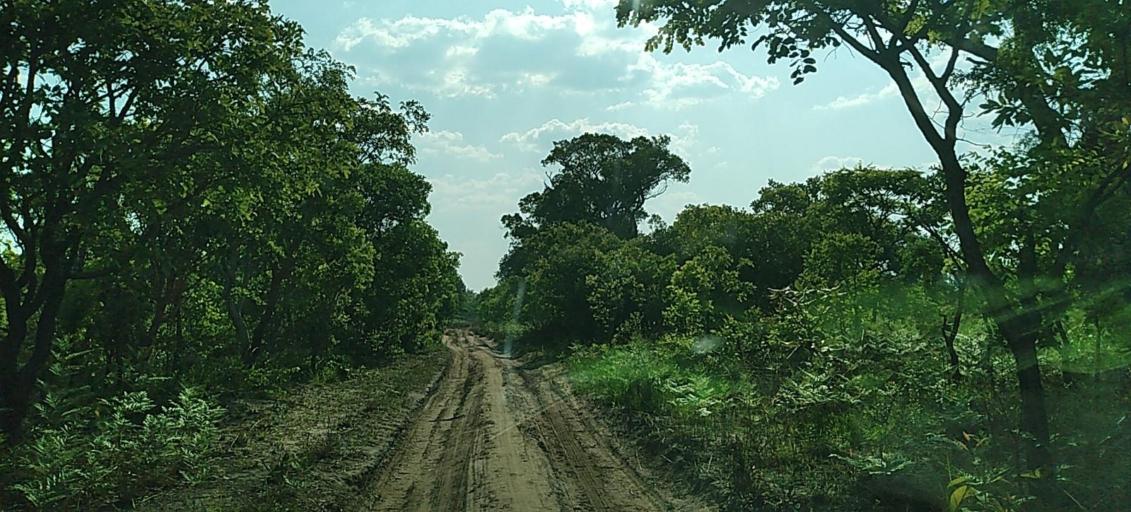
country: ZM
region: North-Western
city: Mwinilunga
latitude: -11.3085
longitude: 24.7858
